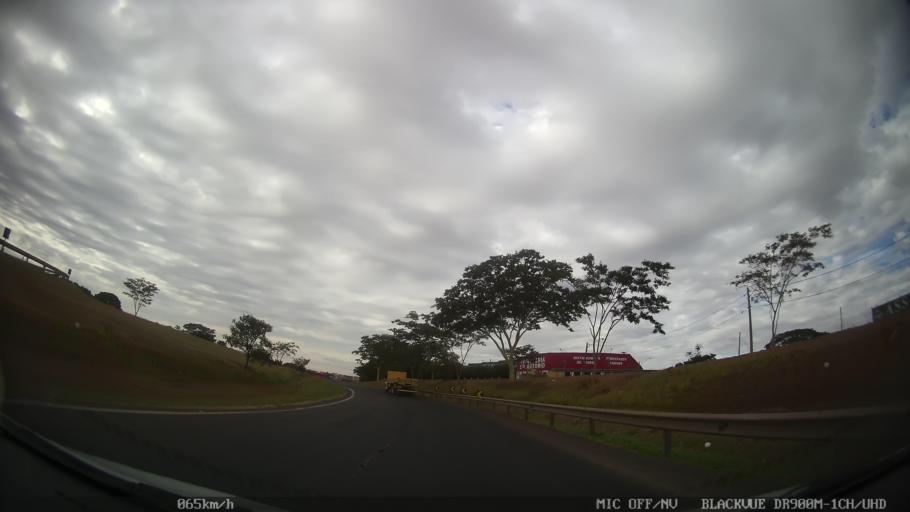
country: BR
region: Sao Paulo
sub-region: Bady Bassitt
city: Bady Bassitt
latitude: -20.8062
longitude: -49.5231
